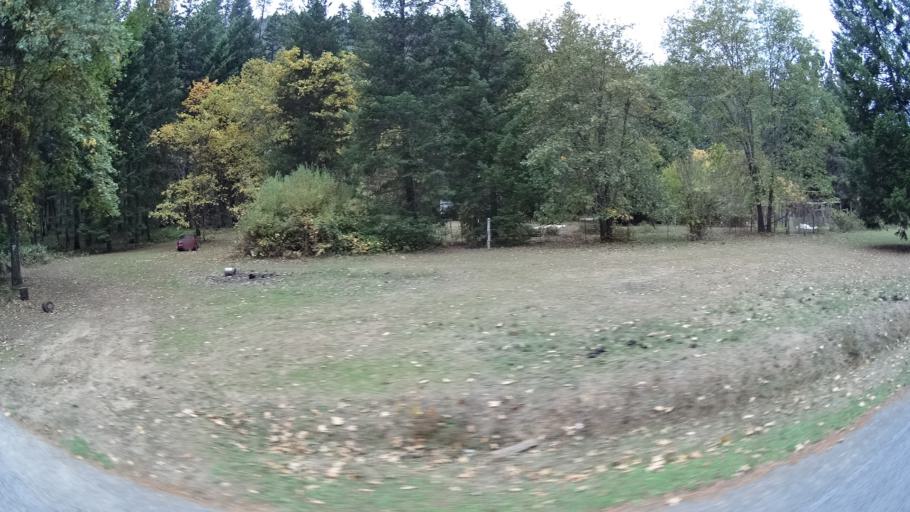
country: US
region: California
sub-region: Siskiyou County
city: Happy Camp
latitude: 41.7880
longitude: -123.3445
